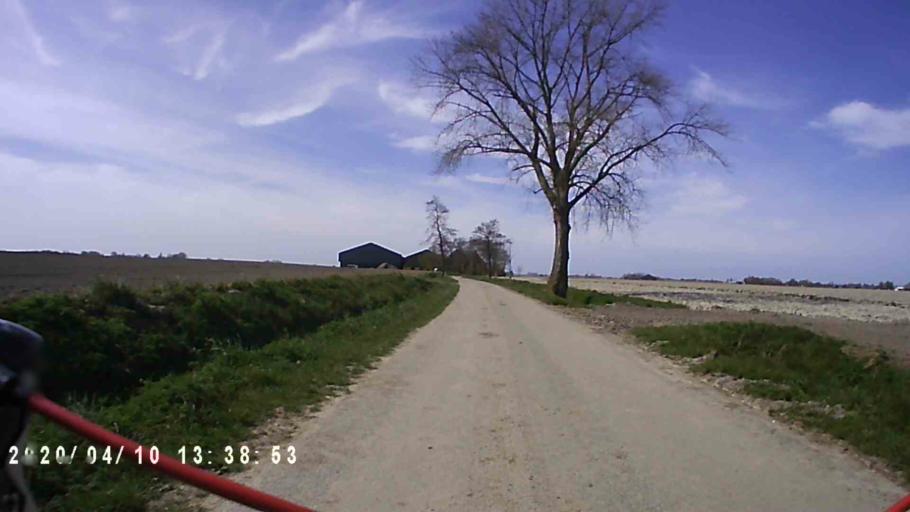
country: NL
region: Groningen
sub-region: Gemeente De Marne
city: Ulrum
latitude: 53.3736
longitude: 6.3946
